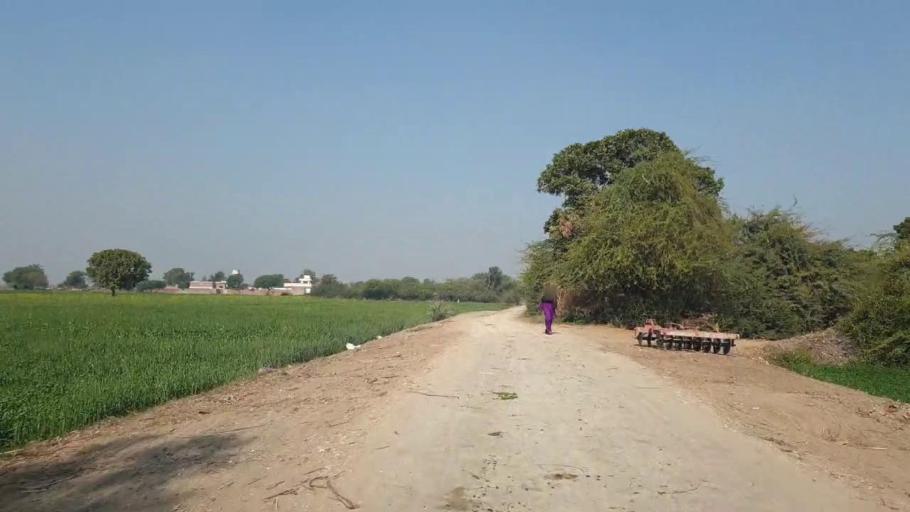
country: PK
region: Sindh
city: Chambar
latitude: 25.3509
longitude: 68.8483
